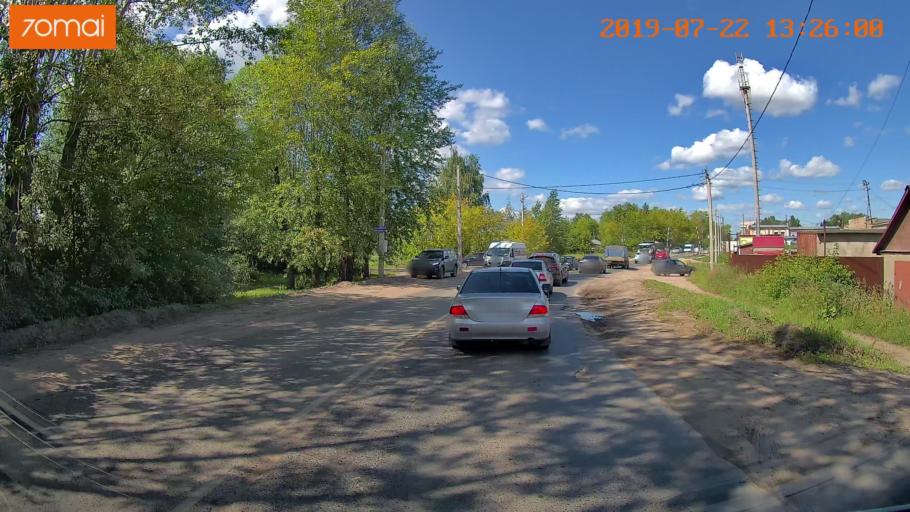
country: RU
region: Ivanovo
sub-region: Gorod Ivanovo
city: Ivanovo
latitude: 57.0280
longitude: 40.9486
